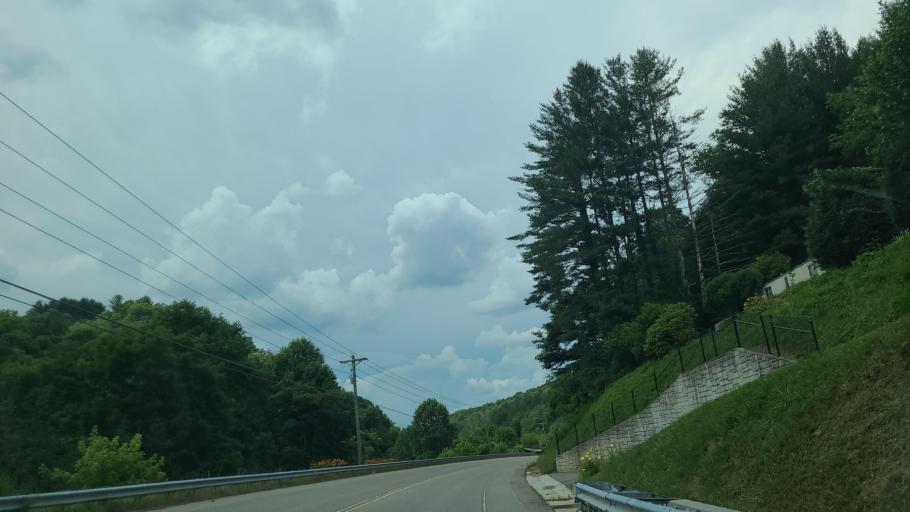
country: US
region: North Carolina
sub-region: Ashe County
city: Jefferson
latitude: 36.3807
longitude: -81.4002
